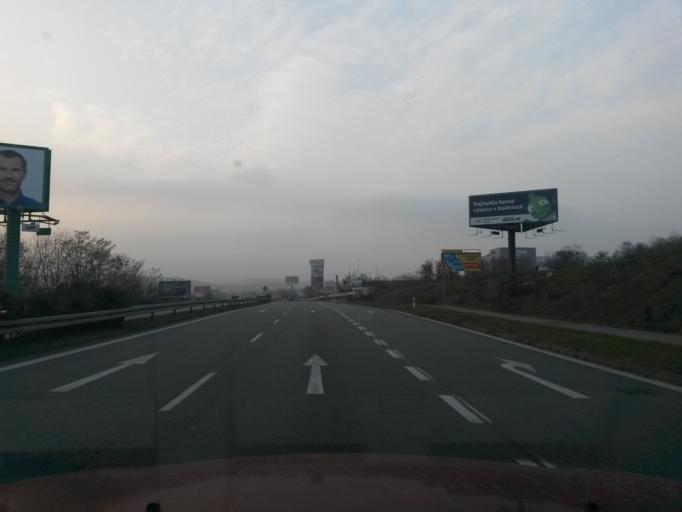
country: SK
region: Kosicky
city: Kosice
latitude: 48.6911
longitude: 21.2429
